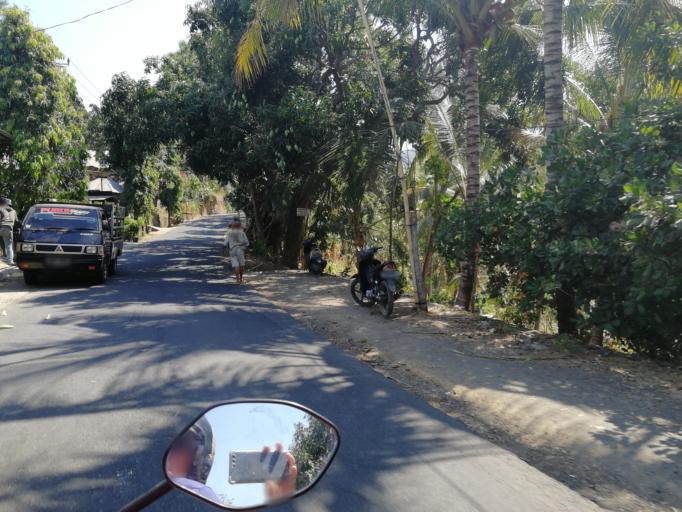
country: ID
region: Bali
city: Banjar Kedisan
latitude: -8.1375
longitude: 115.3221
